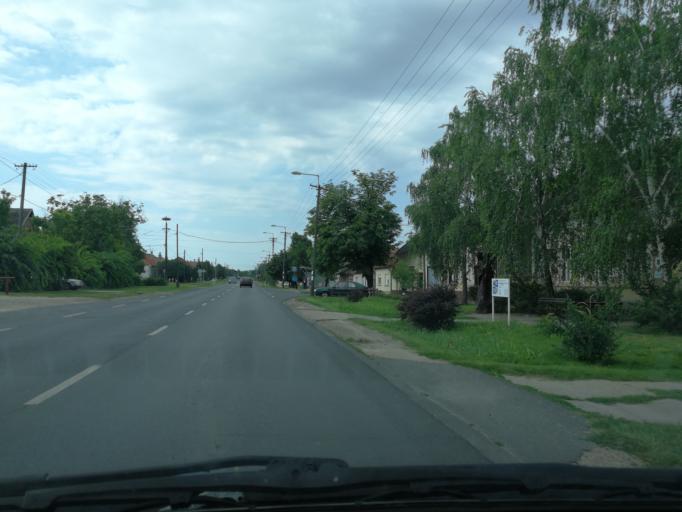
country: HU
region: Bacs-Kiskun
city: Ersekcsanad
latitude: 46.2514
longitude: 18.9786
